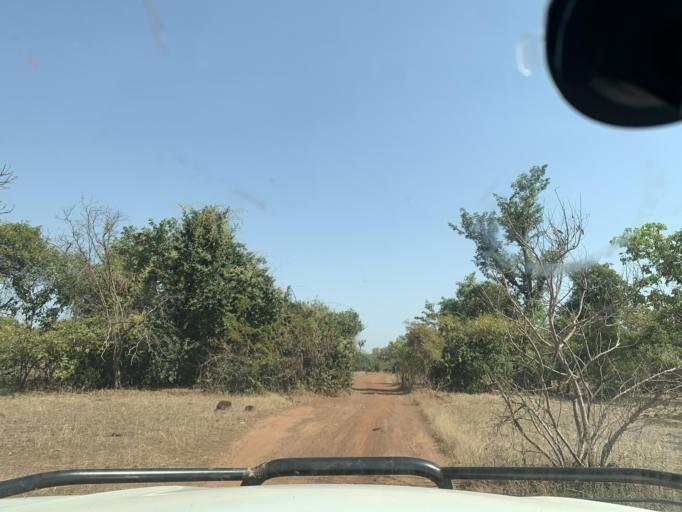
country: ML
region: Sikasso
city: Kolondieba
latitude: 10.8962
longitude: -6.7440
